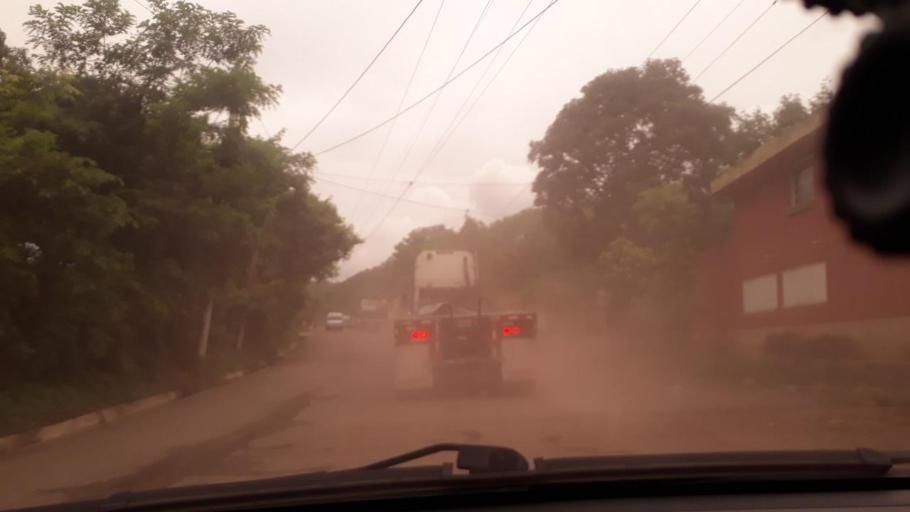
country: GT
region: Chiquimula
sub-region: Municipio de San Juan Ermita
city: San Juan Ermita
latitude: 14.7690
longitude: -89.4273
